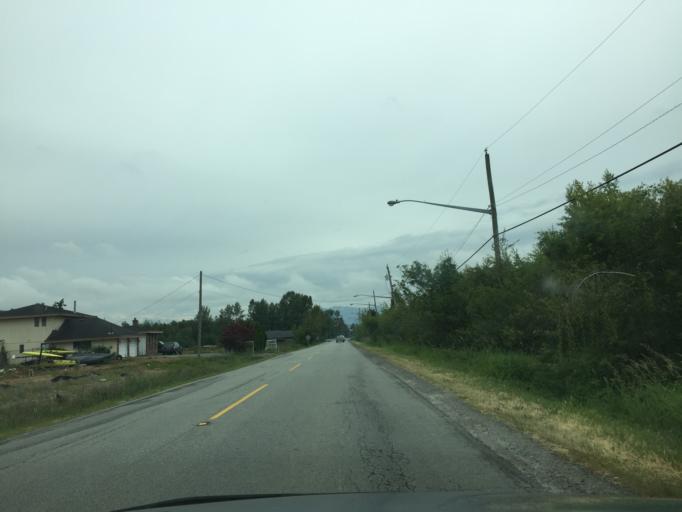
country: CA
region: British Columbia
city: Richmond
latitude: 49.1675
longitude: -123.0806
